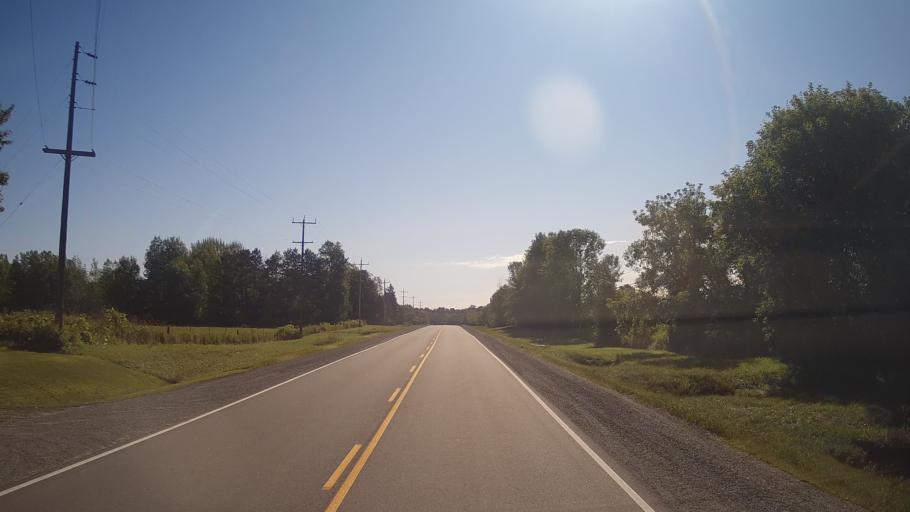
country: CA
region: Ontario
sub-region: Lanark County
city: Smiths Falls
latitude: 44.6262
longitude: -76.0027
